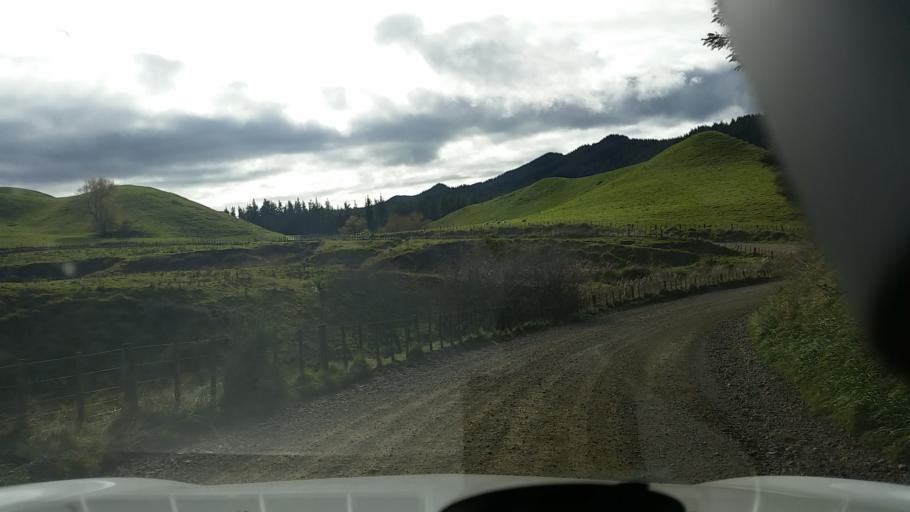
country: NZ
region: Hawke's Bay
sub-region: Napier City
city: Napier
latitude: -39.1069
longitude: 176.8897
